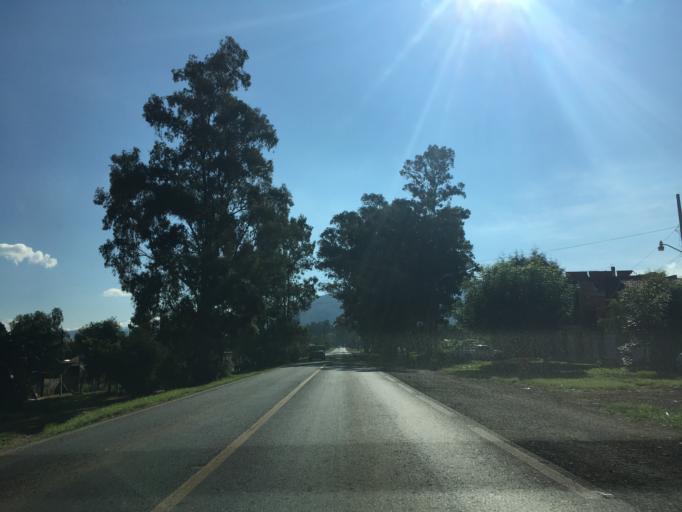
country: MX
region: Mexico
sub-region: Chalco
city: Santo Tomas
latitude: 19.8439
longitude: -102.0876
